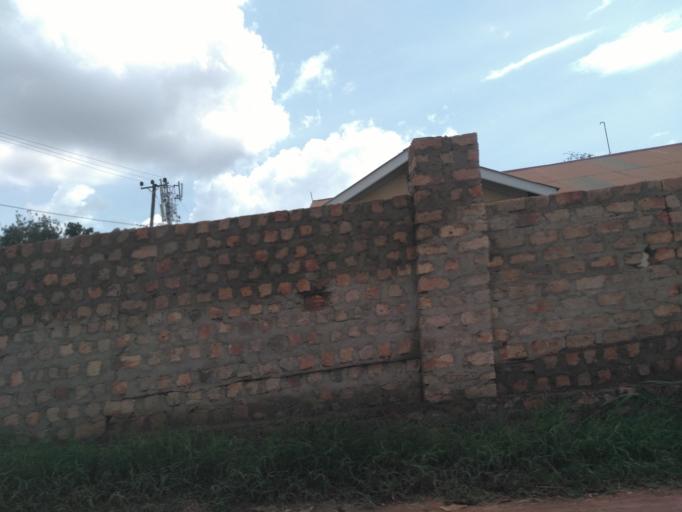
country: UG
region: Central Region
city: Kampala Central Division
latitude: 0.3532
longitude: 32.5814
